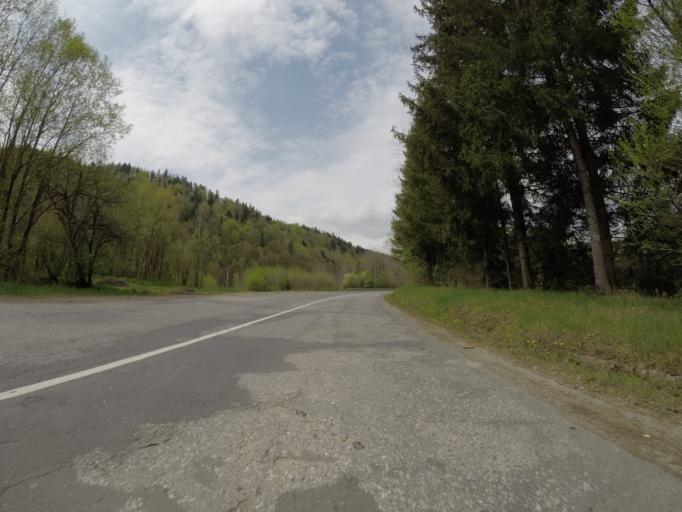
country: SK
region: Banskobystricky
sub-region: Okres Banska Bystrica
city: Brezno
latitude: 48.8184
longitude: 19.7087
